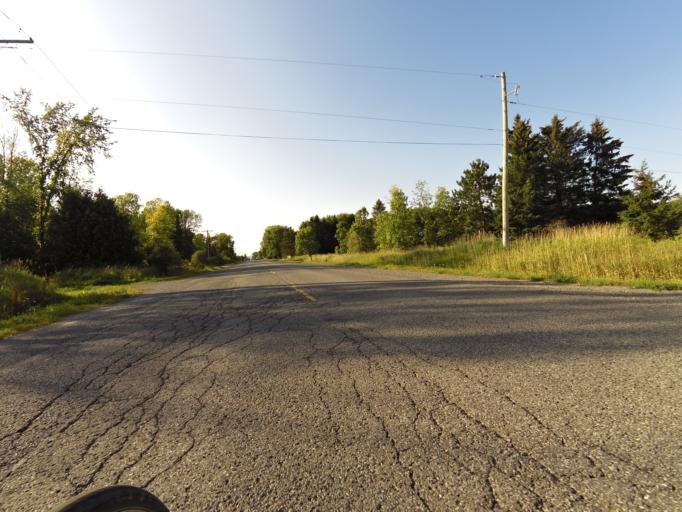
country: CA
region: Ontario
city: Bells Corners
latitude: 45.4587
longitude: -75.9965
